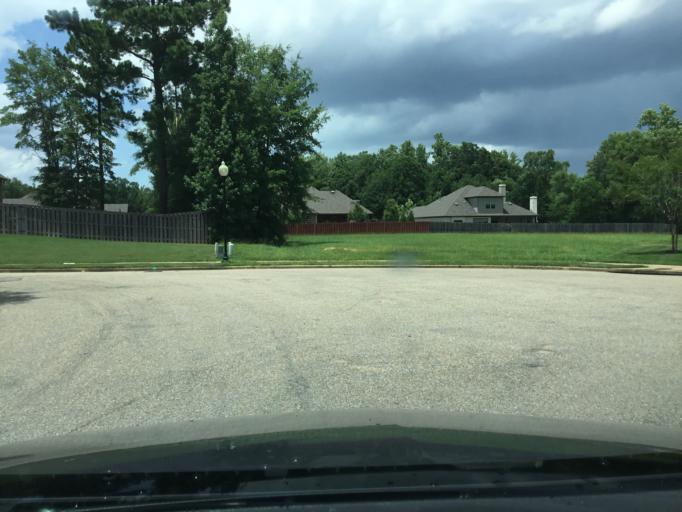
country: US
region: Alabama
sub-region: Montgomery County
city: Pike Road
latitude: 32.3413
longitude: -86.0850
